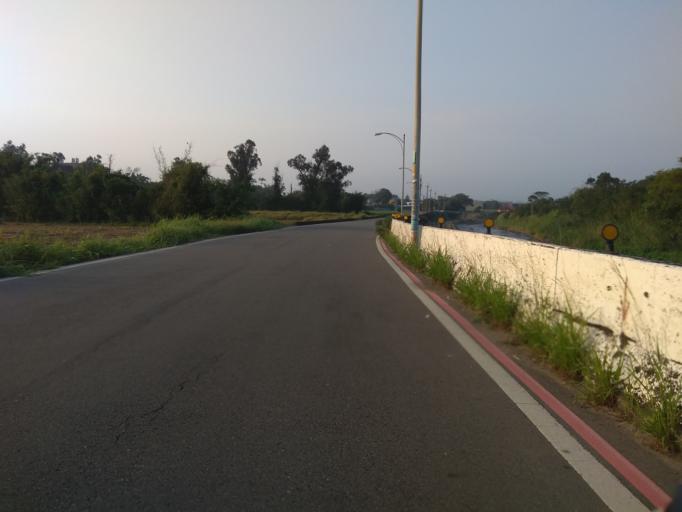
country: TW
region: Taiwan
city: Daxi
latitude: 24.9382
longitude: 121.2118
